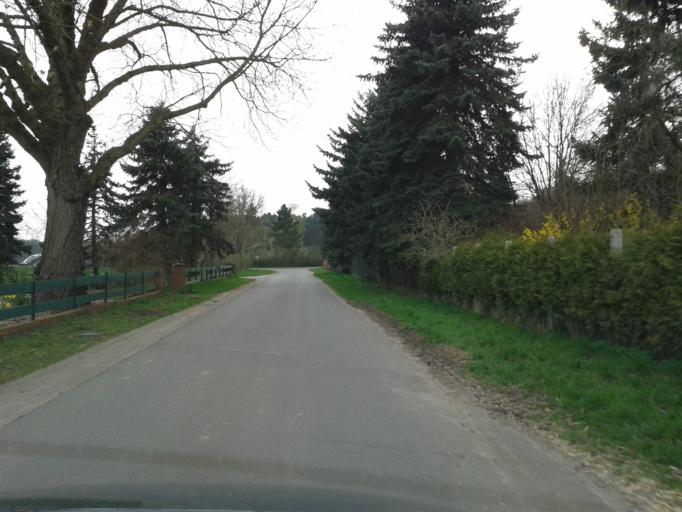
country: DE
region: Lower Saxony
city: Woltersdorf
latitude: 52.9180
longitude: 11.2230
